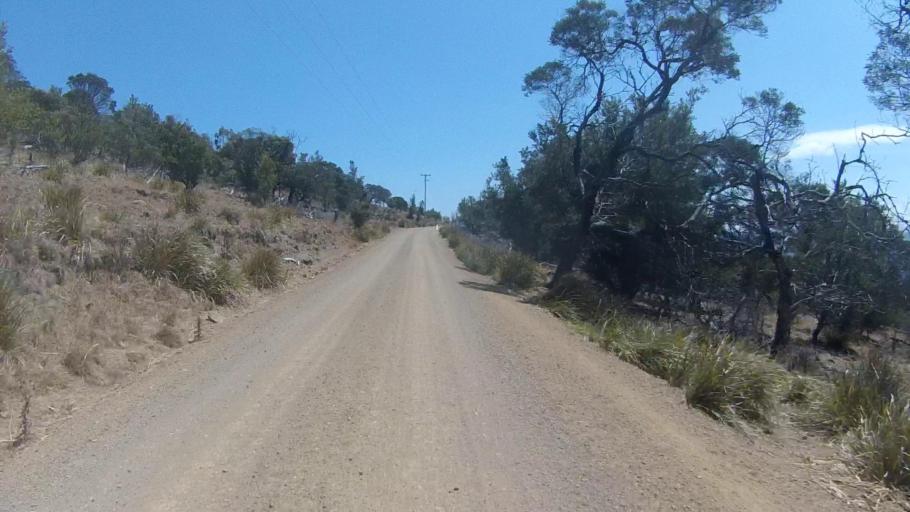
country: AU
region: Tasmania
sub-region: Sorell
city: Sorell
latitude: -42.8931
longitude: 147.8578
